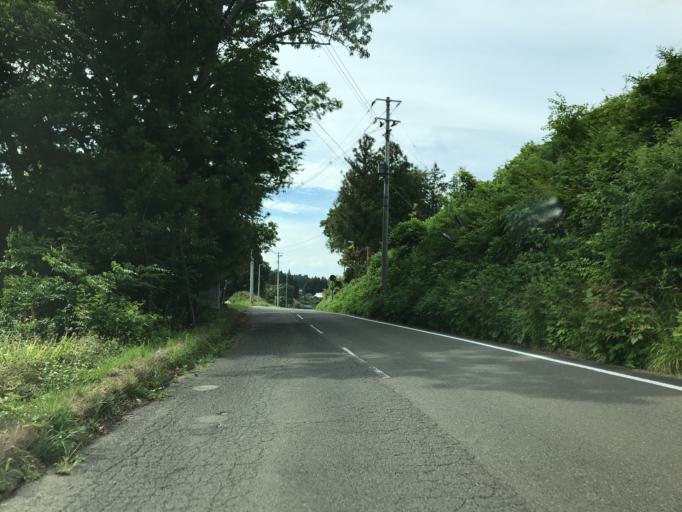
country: JP
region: Fukushima
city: Funehikimachi-funehiki
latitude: 37.5286
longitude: 140.5595
